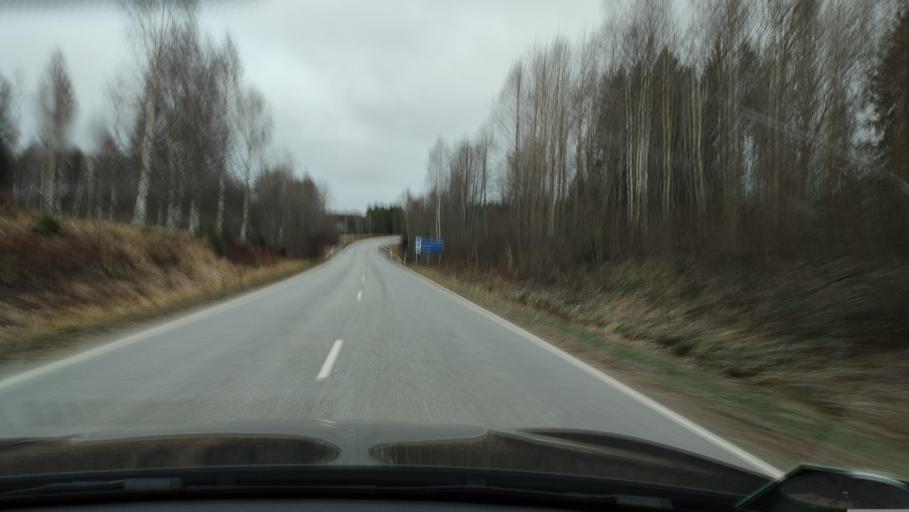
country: FI
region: Southern Ostrobothnia
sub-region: Suupohja
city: Karijoki
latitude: 62.2344
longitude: 21.7481
